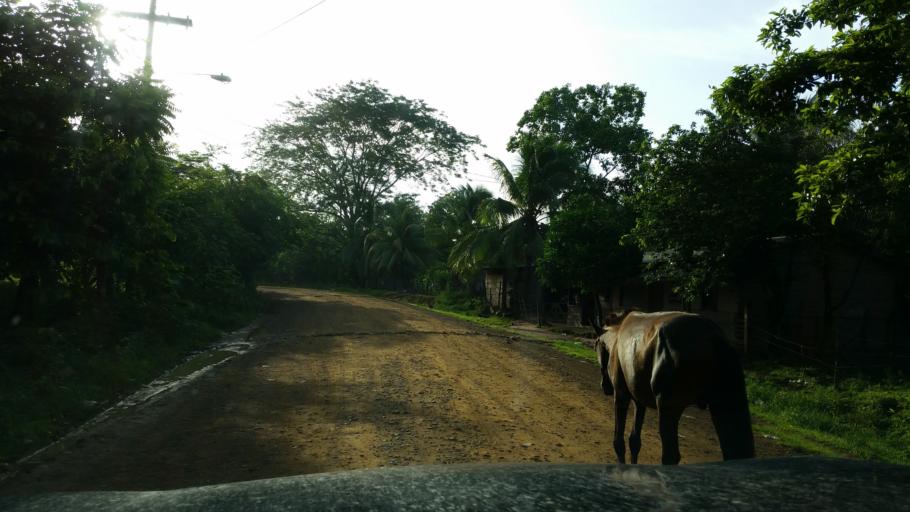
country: NI
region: Atlantico Norte (RAAN)
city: Puerto Cabezas
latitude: 14.0673
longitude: -83.9852
